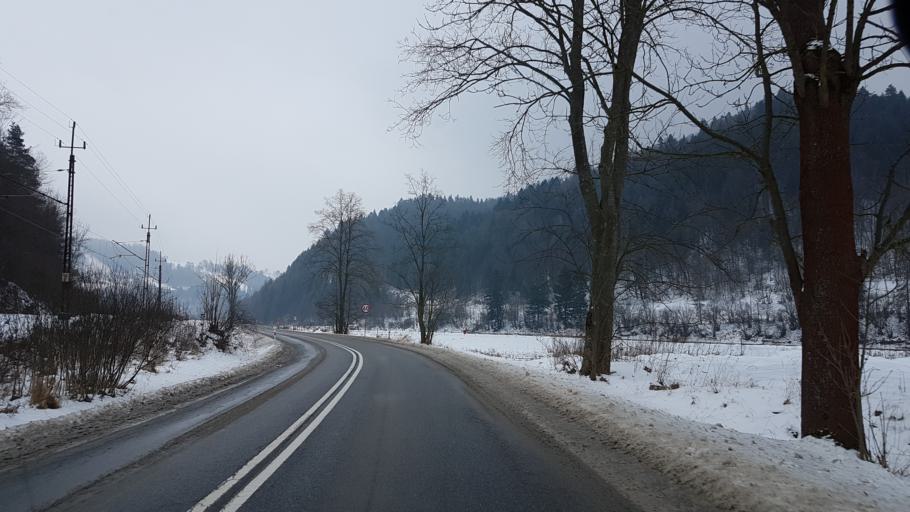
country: PL
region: Lesser Poland Voivodeship
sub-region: Powiat nowosadecki
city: Piwniczna-Zdroj
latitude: 49.3906
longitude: 20.7491
